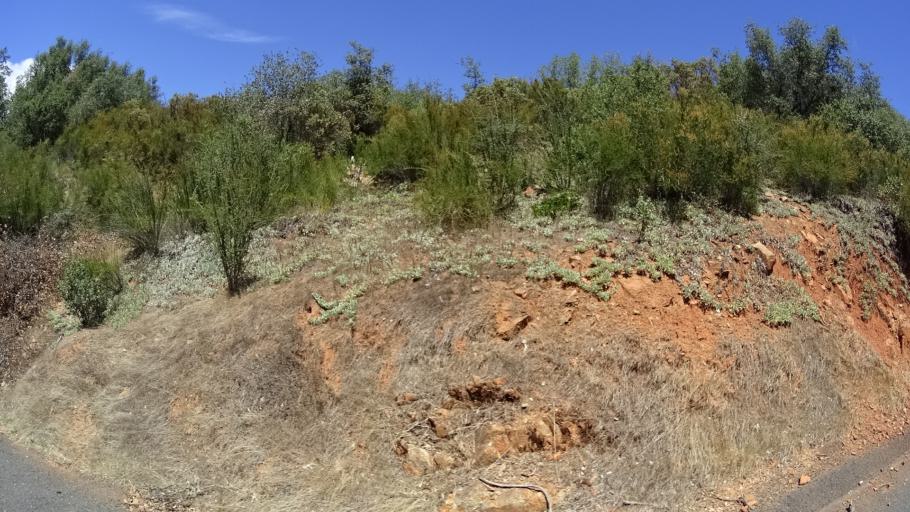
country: US
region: California
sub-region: Calaveras County
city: Forest Meadows
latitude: 38.2168
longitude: -120.4654
